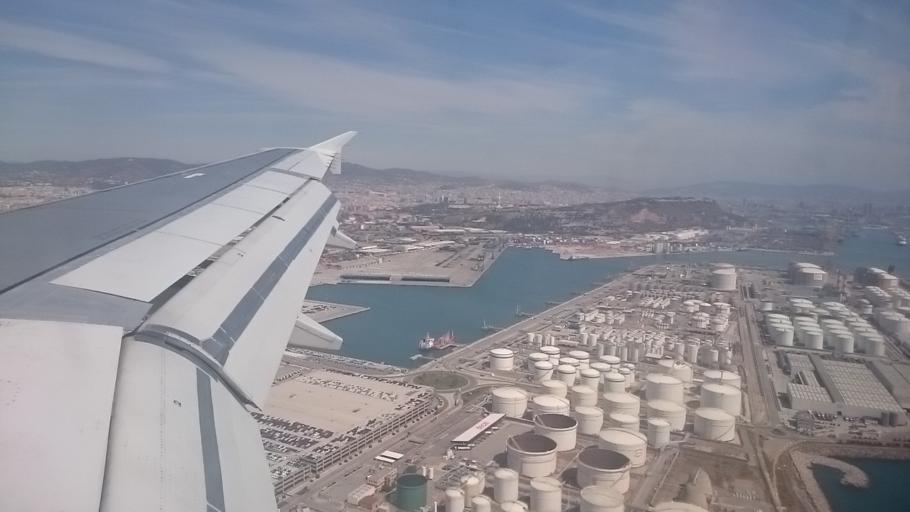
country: ES
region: Catalonia
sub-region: Provincia de Barcelona
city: Sants-Montjuic
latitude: 41.3223
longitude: 2.1502
